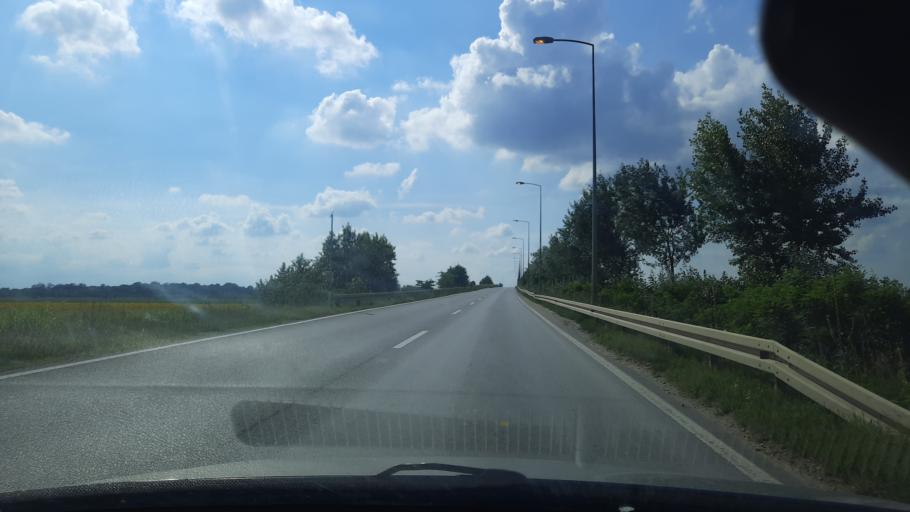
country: RS
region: Central Serbia
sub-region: Branicevski Okrug
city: Pozarevac
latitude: 44.5960
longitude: 21.1588
